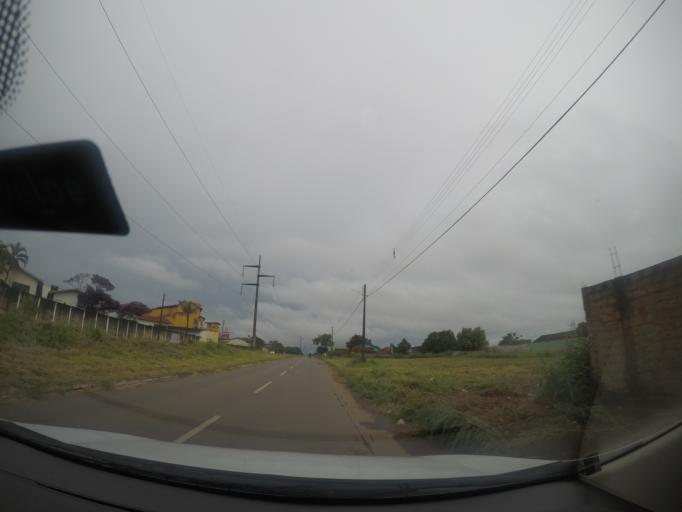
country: BR
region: Goias
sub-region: Aparecida De Goiania
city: Aparecida de Goiania
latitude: -16.7587
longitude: -49.3111
